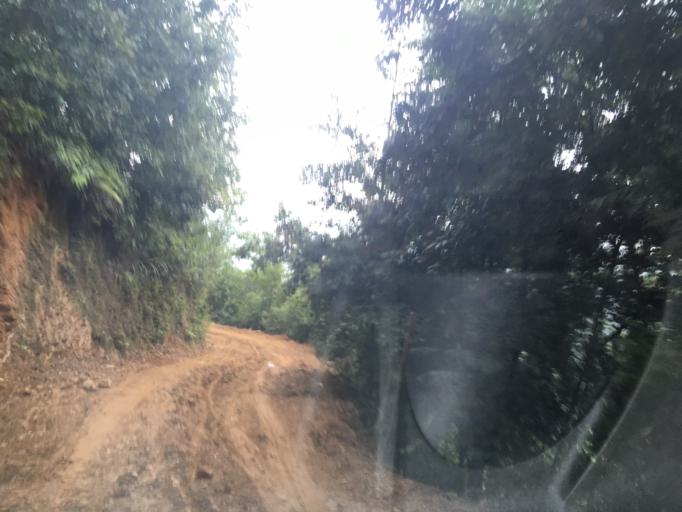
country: CN
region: Guangxi Zhuangzu Zizhiqu
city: Xinzhou
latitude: 25.1647
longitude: 105.6852
